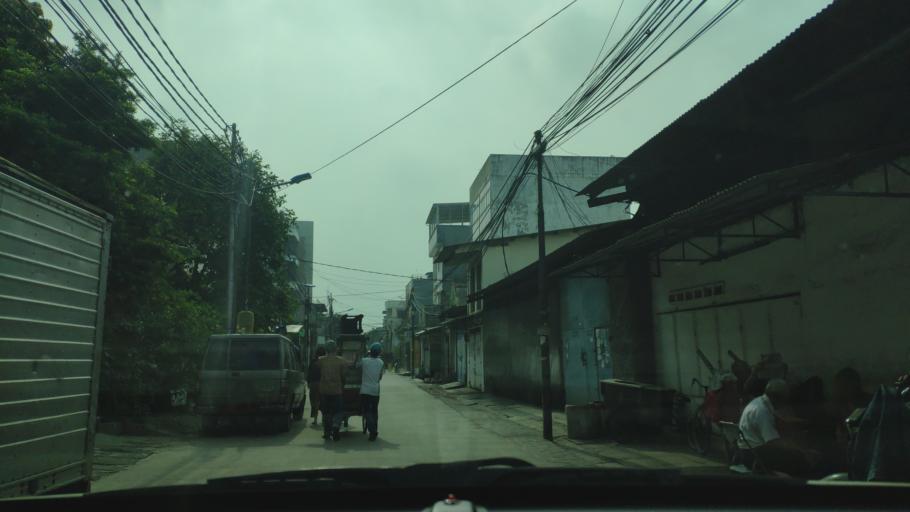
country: ID
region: Jakarta Raya
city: Jakarta
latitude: -6.1585
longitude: 106.8182
